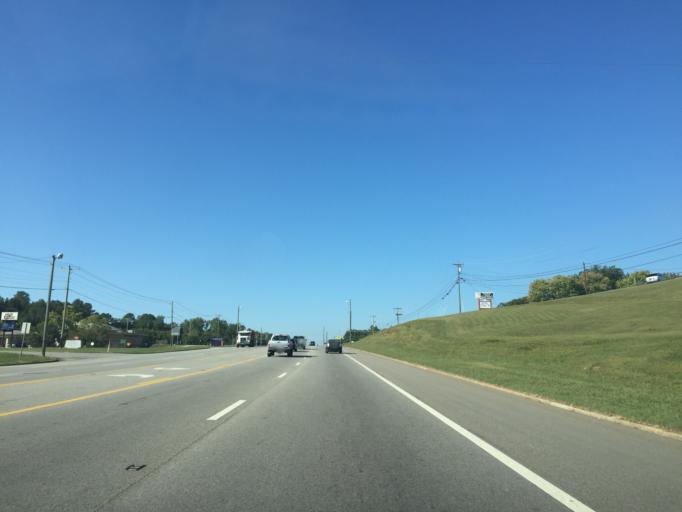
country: US
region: Tennessee
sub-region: Hamilton County
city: Harrison
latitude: 35.1117
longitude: -85.1373
